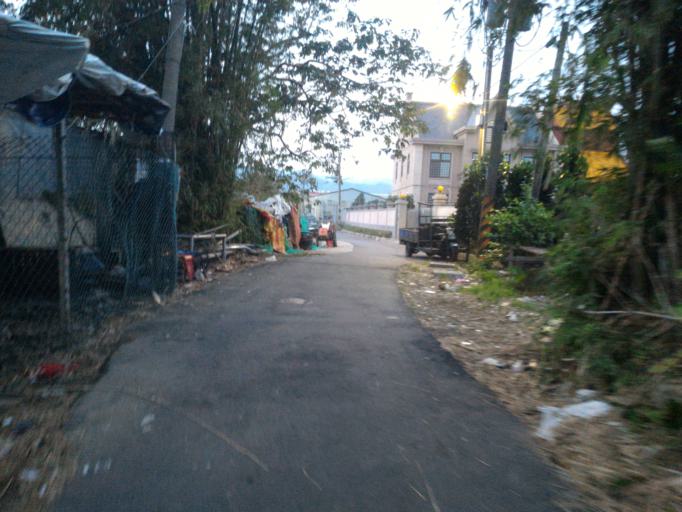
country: TW
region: Taipei
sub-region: Taipei
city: Banqiao
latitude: 24.9556
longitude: 121.4032
